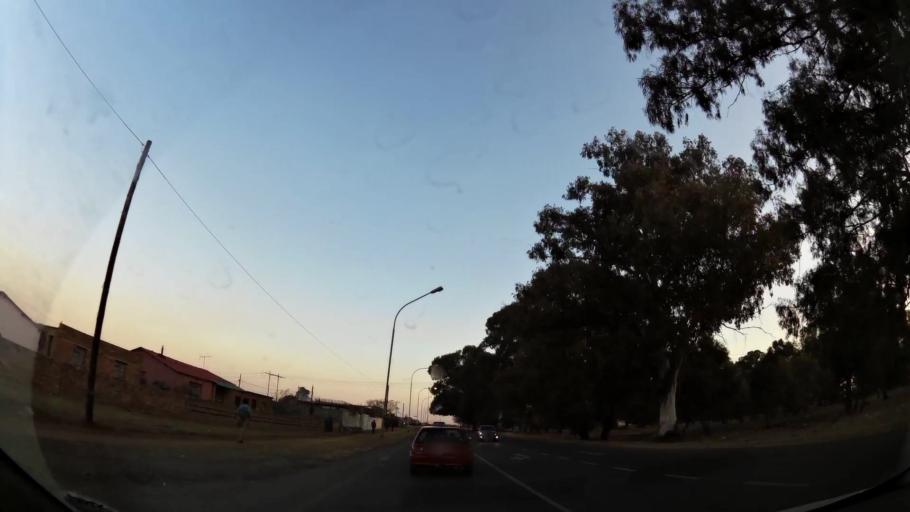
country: ZA
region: Gauteng
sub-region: Ekurhuleni Metropolitan Municipality
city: Springs
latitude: -26.2829
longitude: 28.4048
